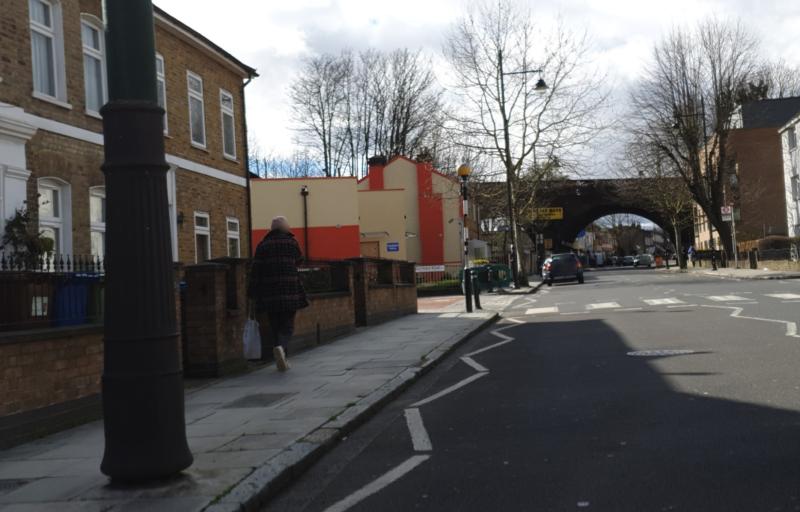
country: GB
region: England
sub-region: Greater London
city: Catford
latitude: 51.4678
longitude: -0.0536
